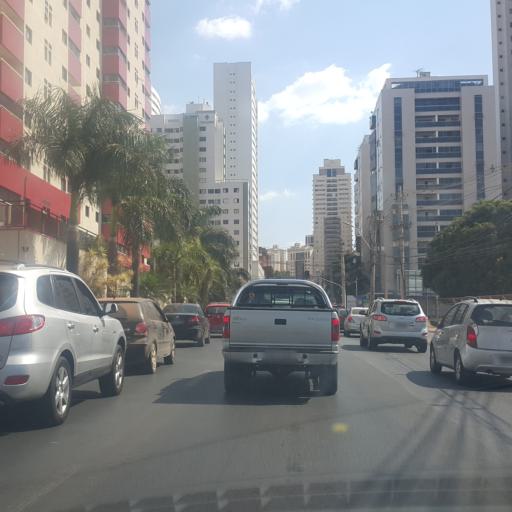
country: BR
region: Federal District
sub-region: Brasilia
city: Brasilia
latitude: -15.8385
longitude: -48.0266
